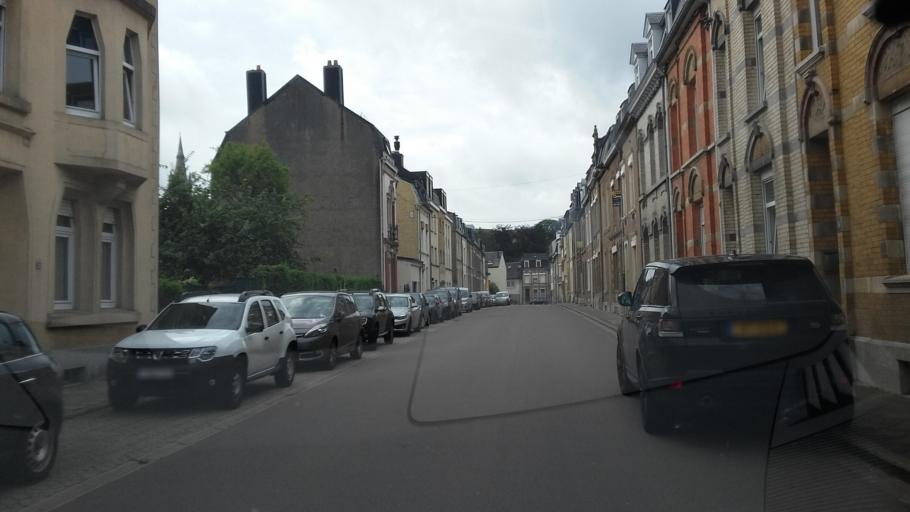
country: BE
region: Wallonia
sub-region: Province du Luxembourg
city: Arlon
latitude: 49.6871
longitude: 5.8068
